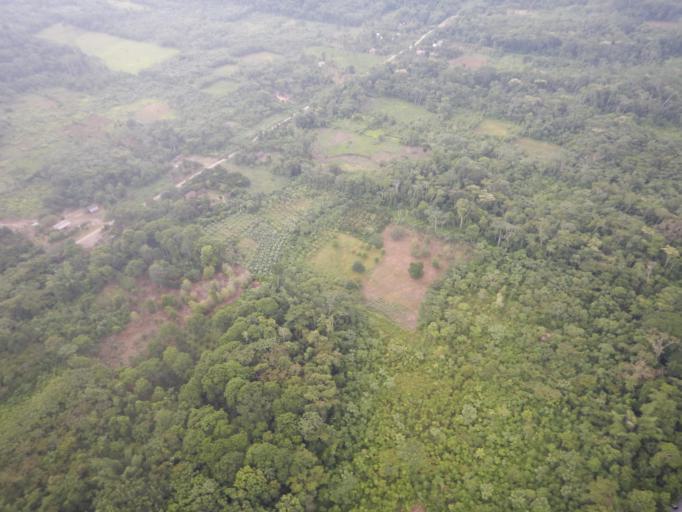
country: BO
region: Cochabamba
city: Chimore
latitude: -17.2336
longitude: -64.6557
